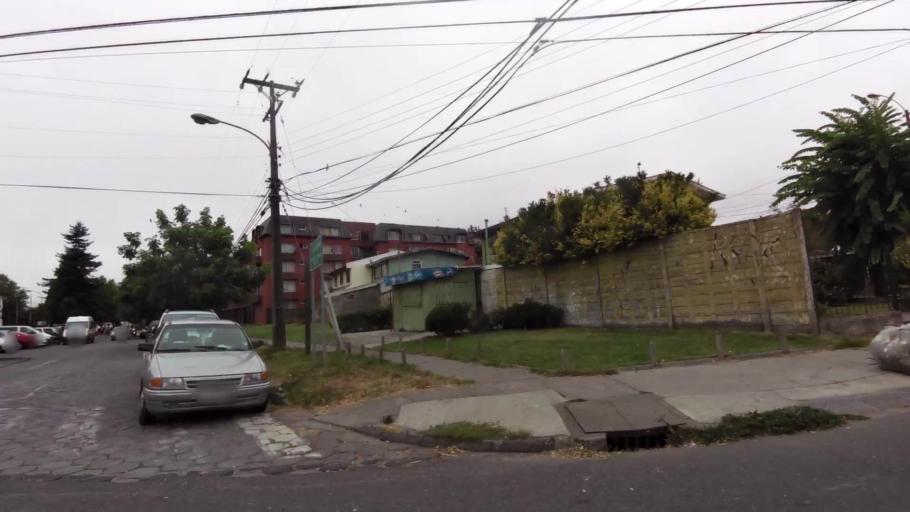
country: CL
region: Biobio
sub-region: Provincia de Concepcion
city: Concepcion
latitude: -36.8140
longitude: -73.0325
